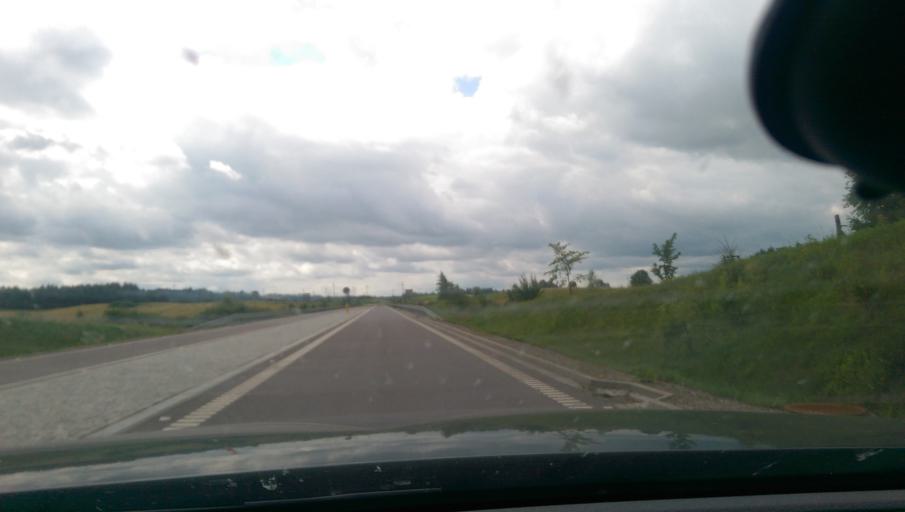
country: PL
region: Warmian-Masurian Voivodeship
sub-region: Powiat goldapski
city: Goldap
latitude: 54.3072
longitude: 22.2796
